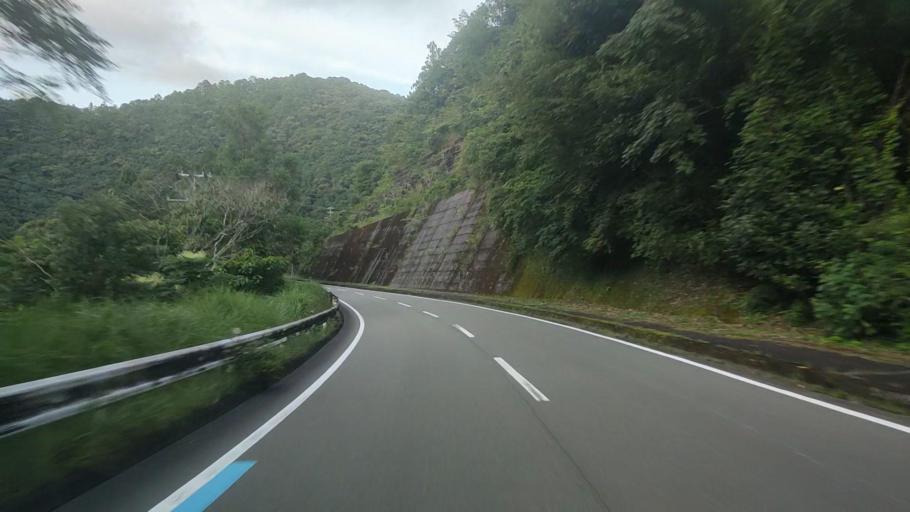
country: JP
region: Wakayama
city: Shingu
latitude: 33.8219
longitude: 135.7743
